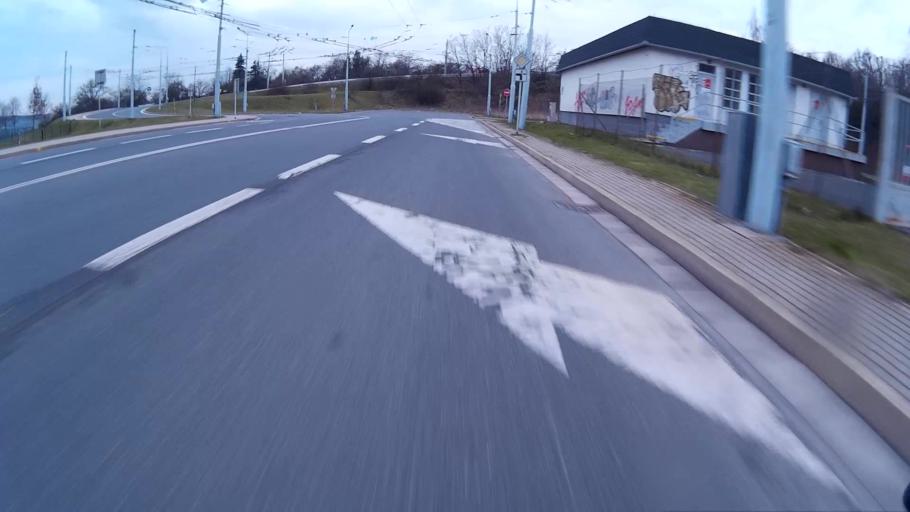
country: CZ
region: South Moravian
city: Ostopovice
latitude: 49.1796
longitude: 16.5466
